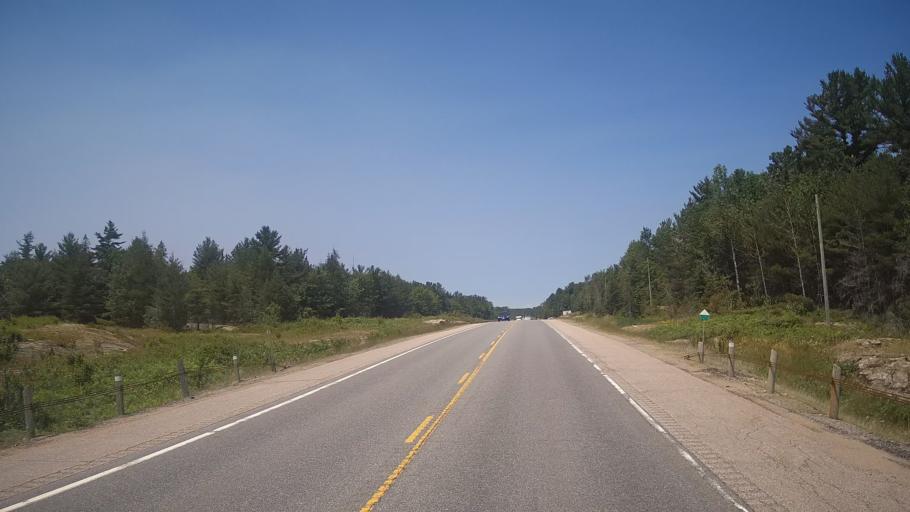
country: CA
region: Ontario
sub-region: Parry Sound District
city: Parry Sound
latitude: 45.4698
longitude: -80.1686
